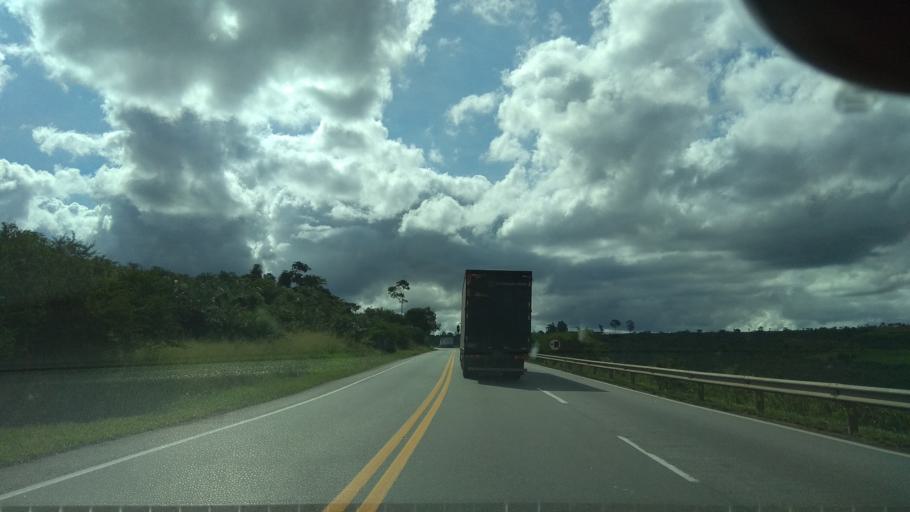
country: BR
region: Bahia
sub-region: Santa Ines
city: Santa Ines
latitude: -13.1162
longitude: -39.9893
